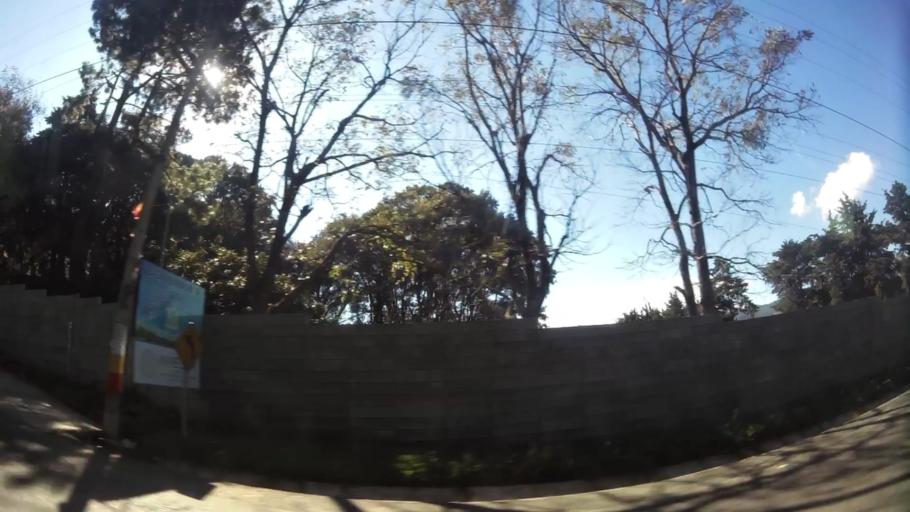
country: GT
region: Sacatepequez
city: Magdalena Milpas Altas
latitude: 14.5639
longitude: -90.6393
